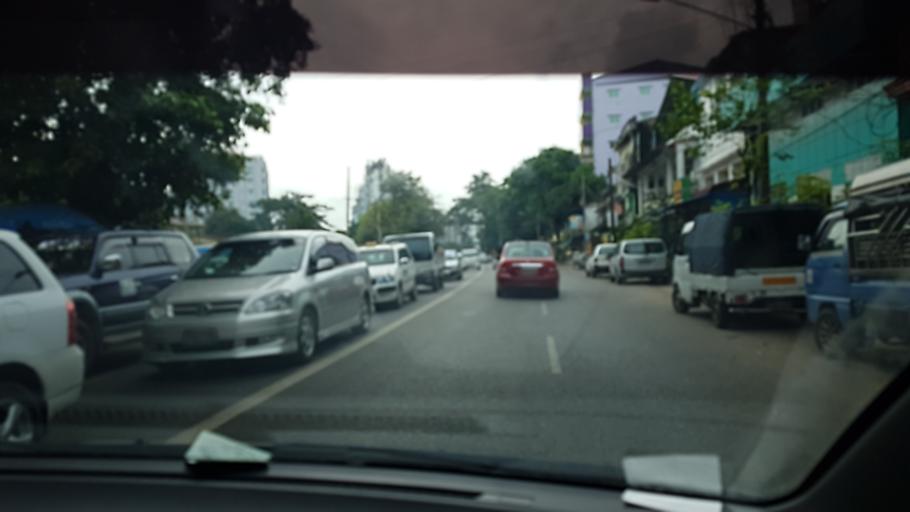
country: MM
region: Yangon
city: Yangon
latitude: 16.8020
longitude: 96.1260
